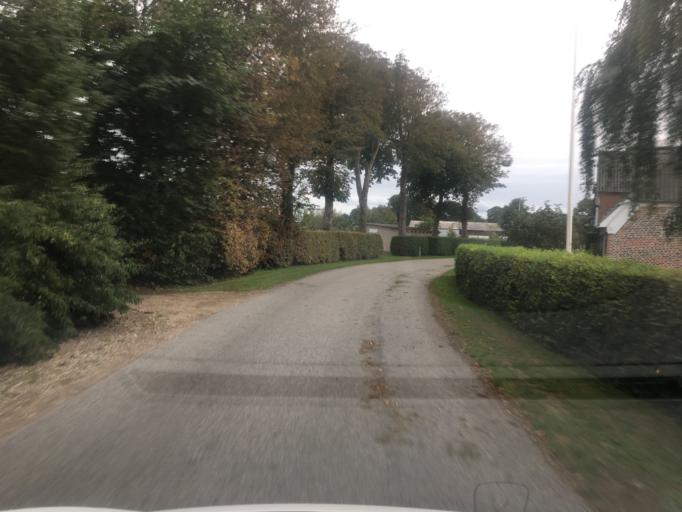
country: DK
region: South Denmark
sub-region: Tonder Kommune
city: Tonder
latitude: 54.9608
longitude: 8.9258
